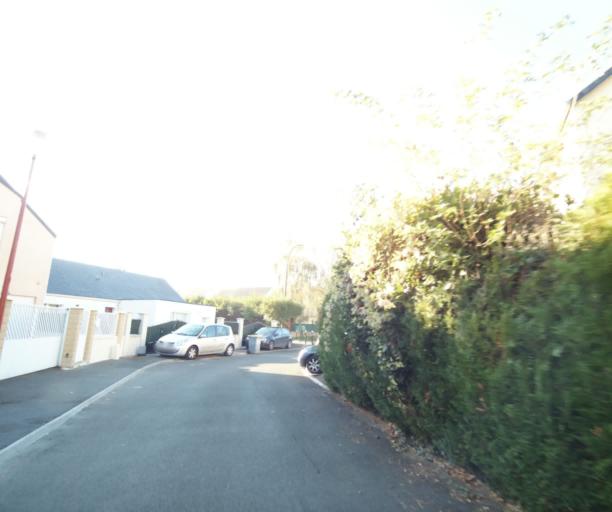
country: FR
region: Ile-de-France
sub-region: Departement du Val-d'Oise
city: Gonesse
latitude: 48.9936
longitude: 2.4325
